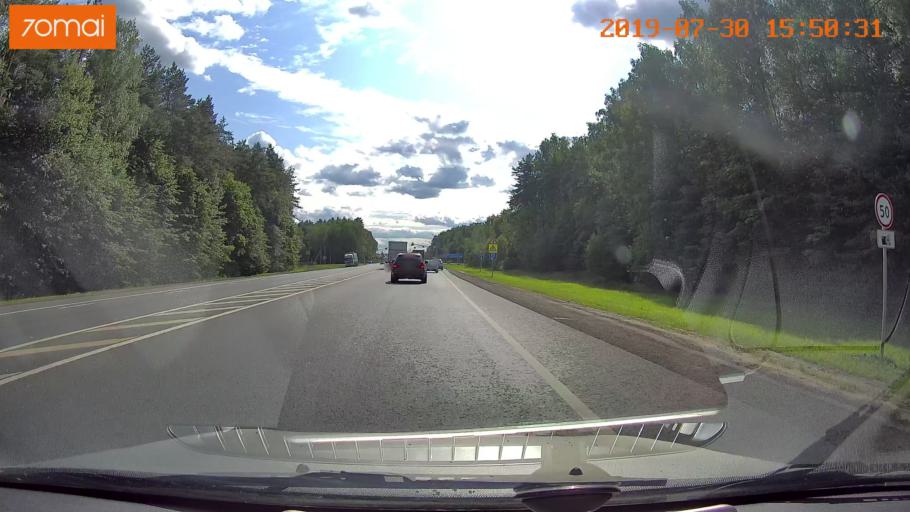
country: RU
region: Moskovskaya
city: Voskresensk
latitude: 55.3311
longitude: 38.6509
